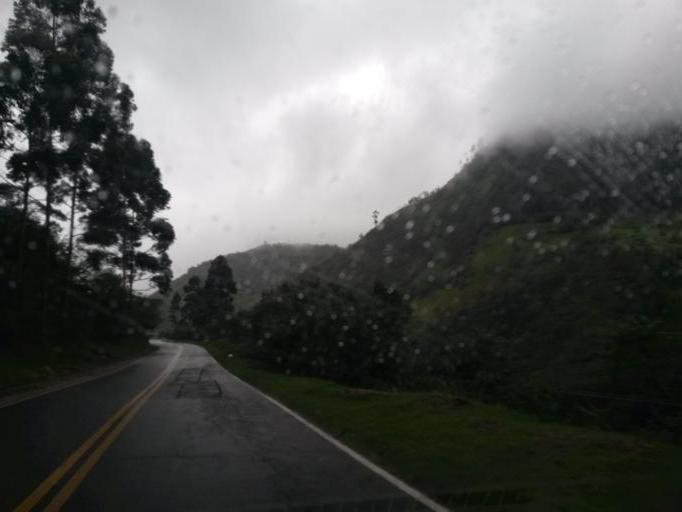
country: CO
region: Cauca
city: Popayan
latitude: 2.3711
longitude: -76.4925
